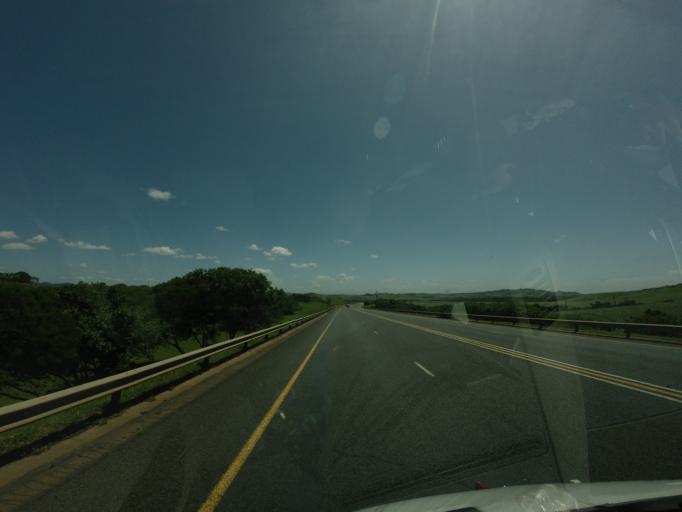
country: ZA
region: KwaZulu-Natal
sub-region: uThungulu District Municipality
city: eSikhawini
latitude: -28.9436
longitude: 31.7463
